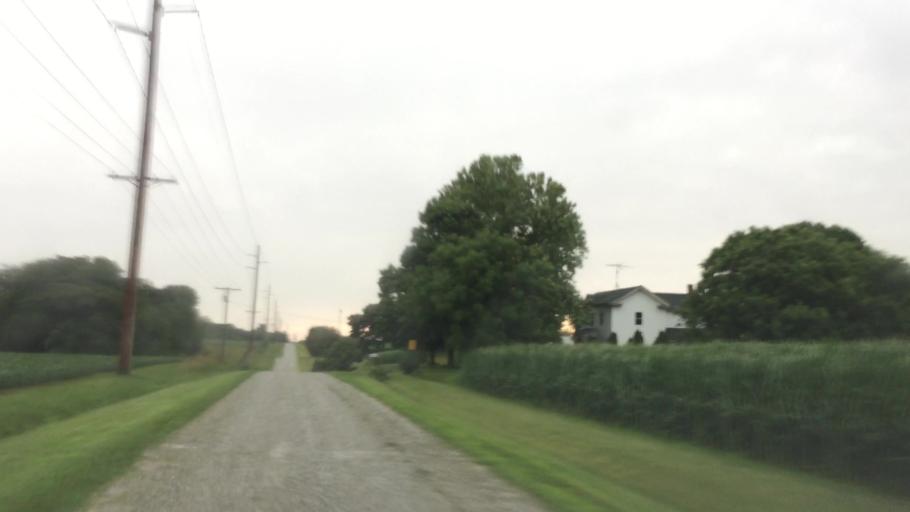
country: US
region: Iowa
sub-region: Lee County
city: Fort Madison
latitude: 40.5974
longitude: -91.2677
